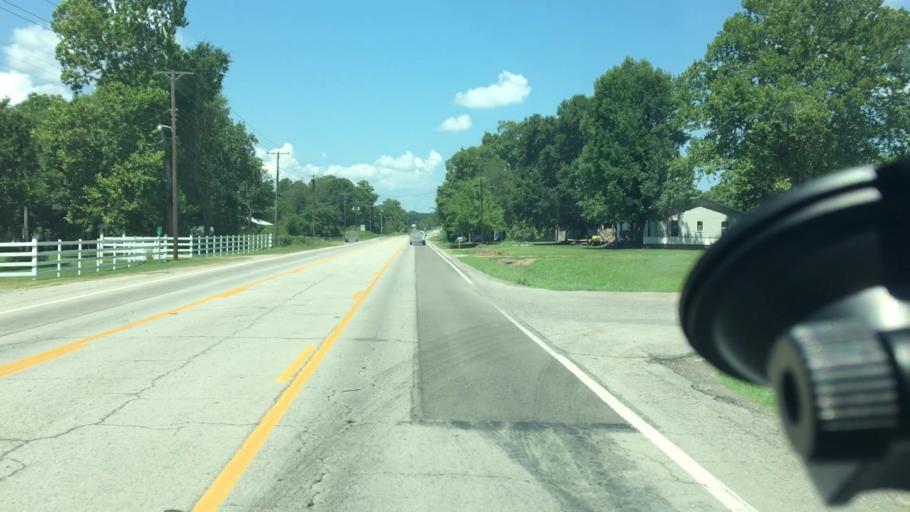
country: US
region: Arkansas
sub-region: Sebastian County
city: Lavaca
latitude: 35.2943
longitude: -94.1403
